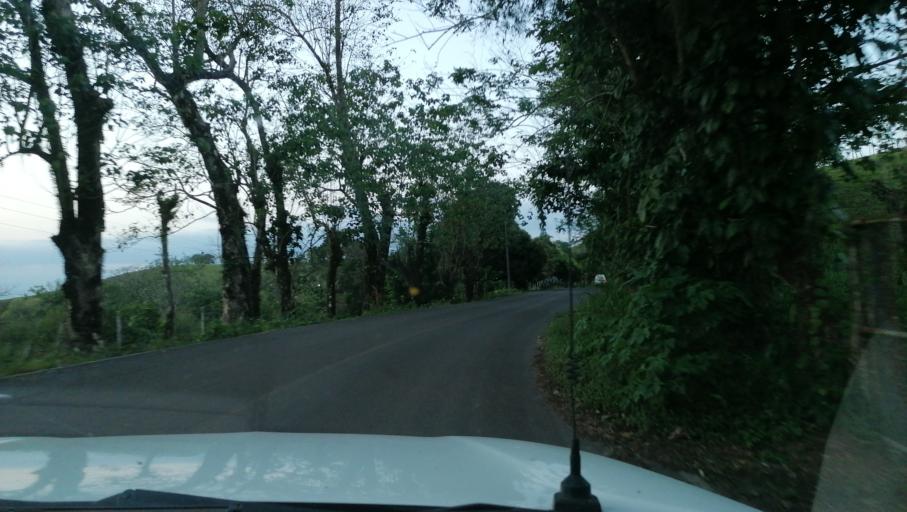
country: MX
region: Chiapas
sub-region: Ostuacan
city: Nuevo Juan del Grijalva
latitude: 17.4278
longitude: -93.3515
